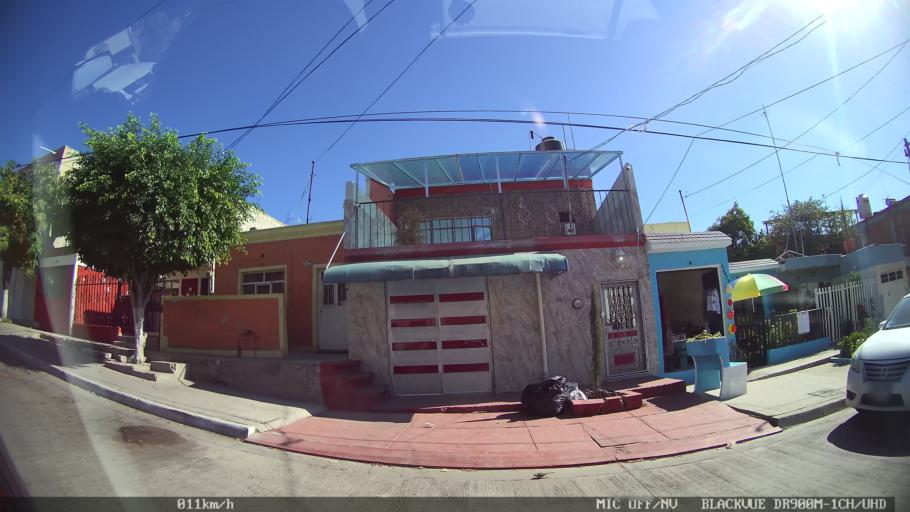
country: MX
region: Jalisco
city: Tlaquepaque
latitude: 20.6849
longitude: -103.2708
